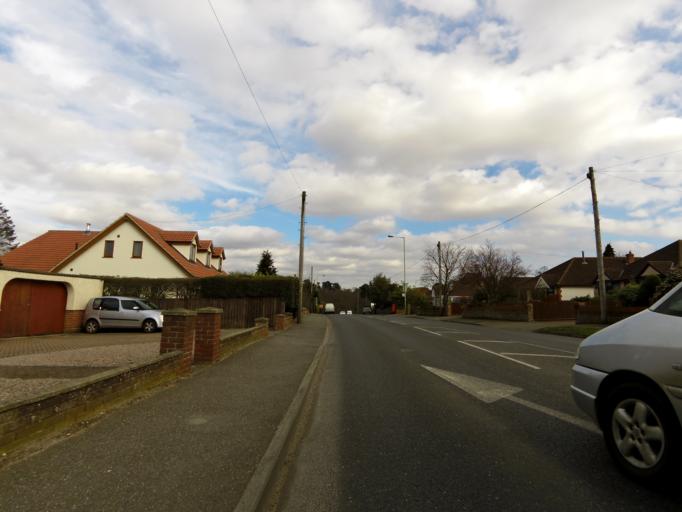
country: GB
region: England
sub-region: Suffolk
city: Kesgrave
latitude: 52.0493
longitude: 1.2201
